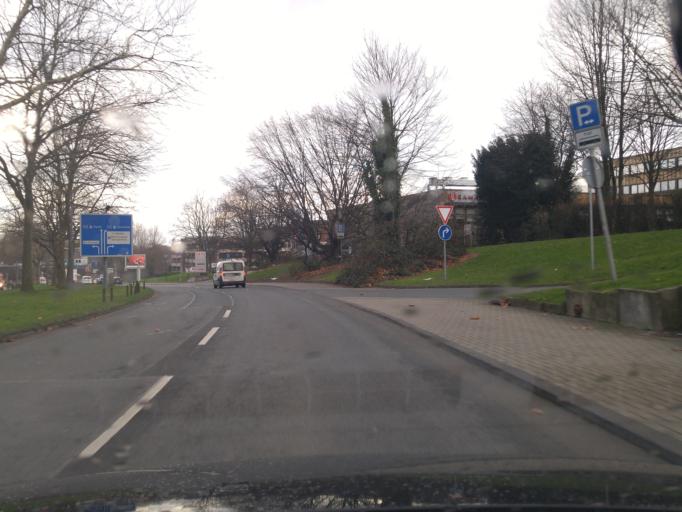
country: DE
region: North Rhine-Westphalia
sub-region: Regierungsbezirk Arnsberg
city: Bochum
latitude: 51.4913
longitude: 7.2328
